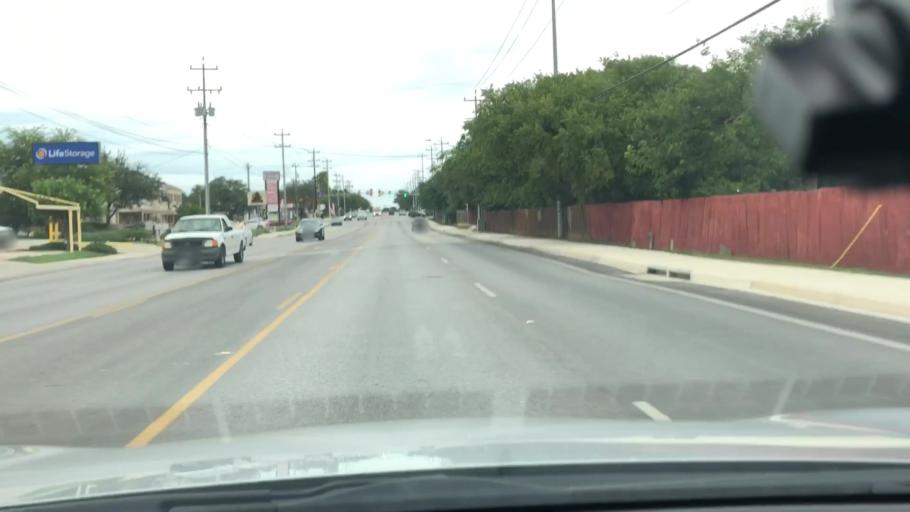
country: US
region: Texas
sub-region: Bexar County
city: Leon Valley
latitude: 29.4883
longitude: -98.6656
